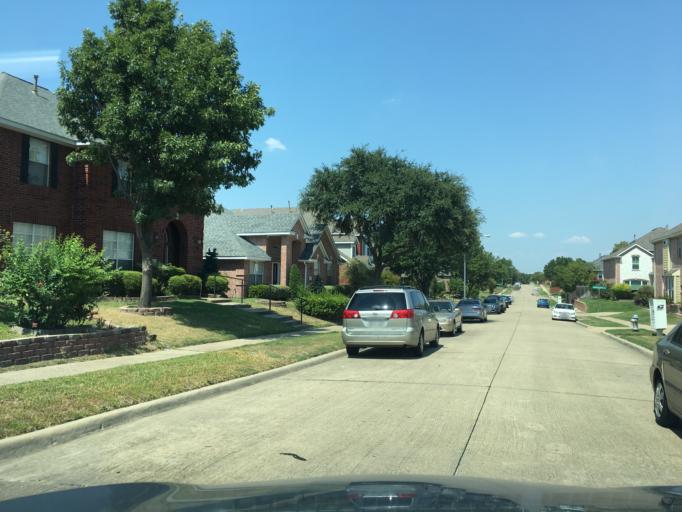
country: US
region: Texas
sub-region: Dallas County
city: Garland
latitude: 32.9619
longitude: -96.6663
